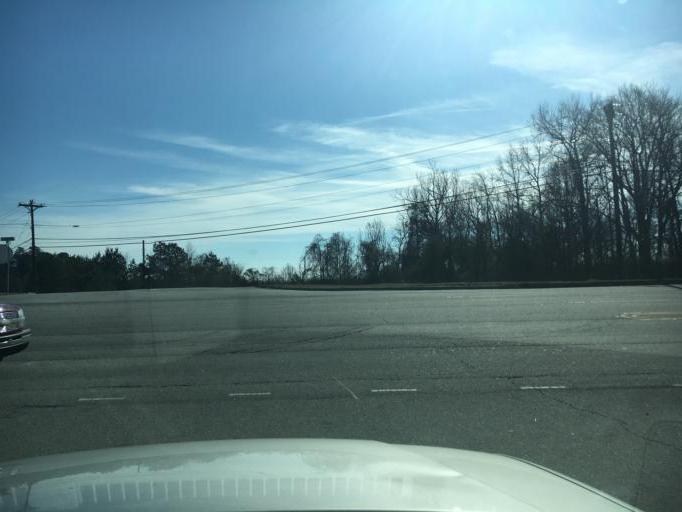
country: US
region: South Carolina
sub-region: Spartanburg County
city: Spartanburg
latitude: 35.0149
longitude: -81.8986
